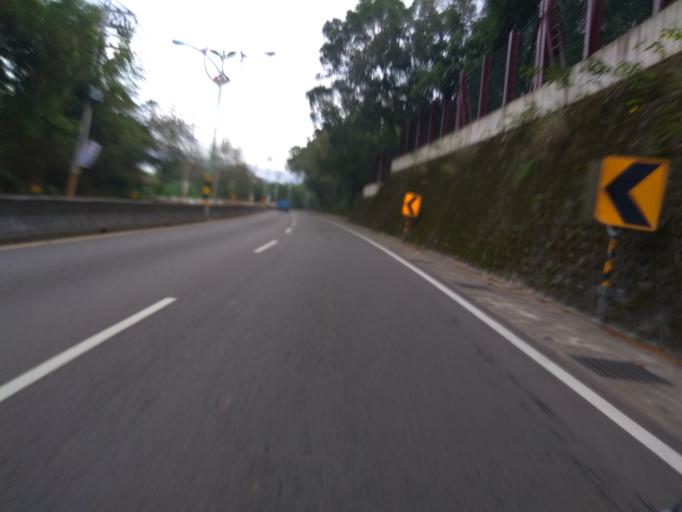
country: TW
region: Taiwan
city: Daxi
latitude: 24.8500
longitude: 121.2057
